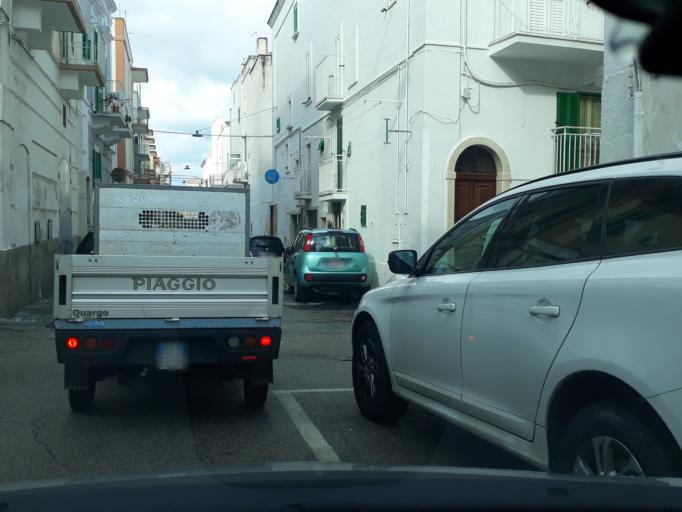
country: IT
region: Apulia
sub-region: Provincia di Brindisi
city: Fasano
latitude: 40.8351
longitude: 17.3571
